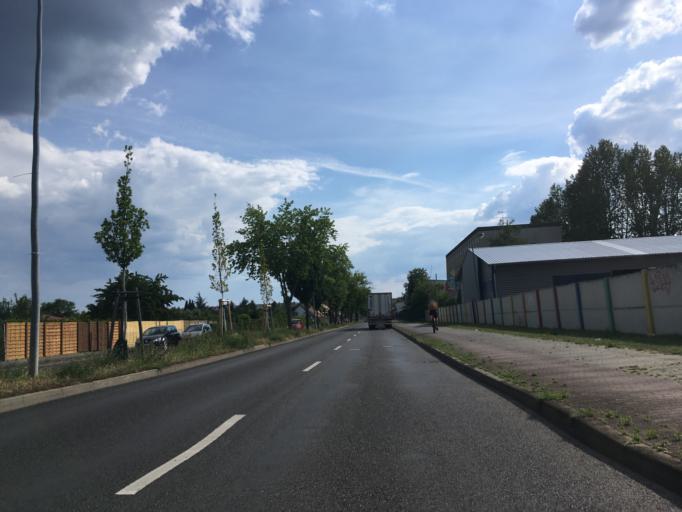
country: DE
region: Brandenburg
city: Furstenwalde
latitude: 52.3763
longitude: 14.0772
